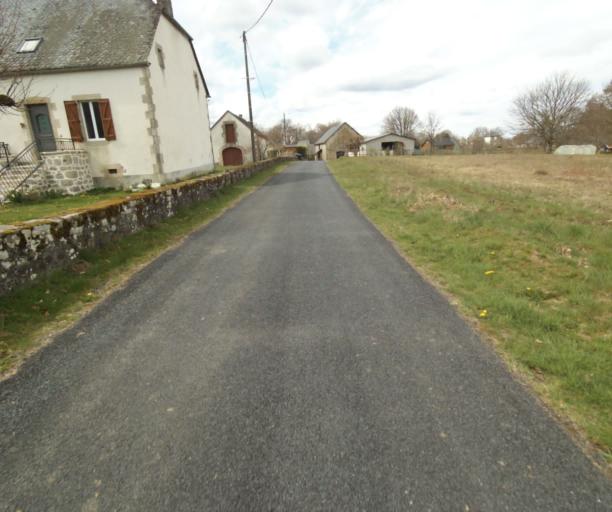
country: FR
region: Limousin
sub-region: Departement de la Correze
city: Argentat
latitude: 45.2190
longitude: 1.9217
